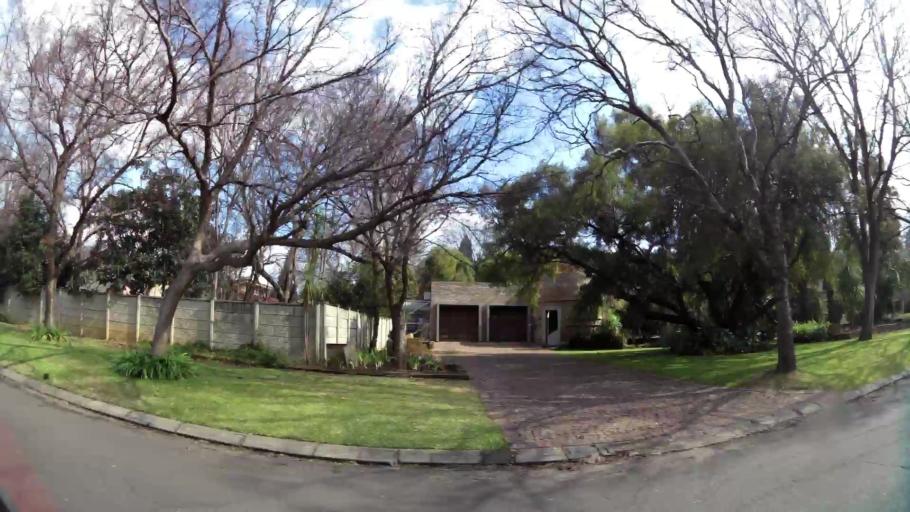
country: ZA
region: Gauteng
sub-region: Sedibeng District Municipality
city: Vanderbijlpark
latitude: -26.7371
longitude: 27.8360
